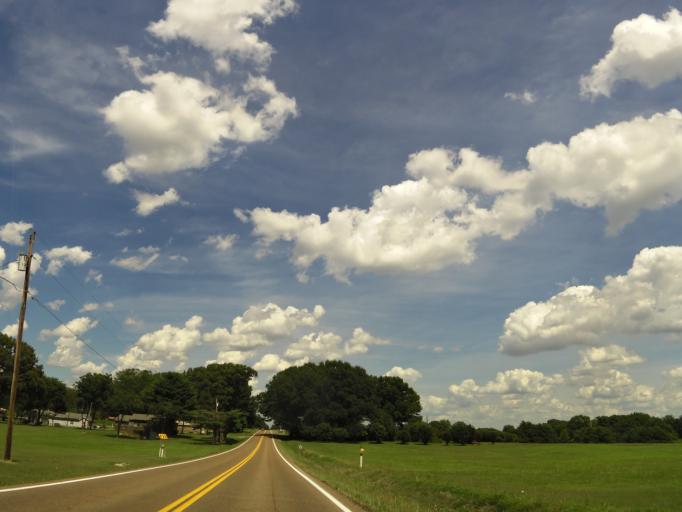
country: US
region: Tennessee
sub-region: Dyer County
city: Newbern
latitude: 36.0289
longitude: -89.2449
